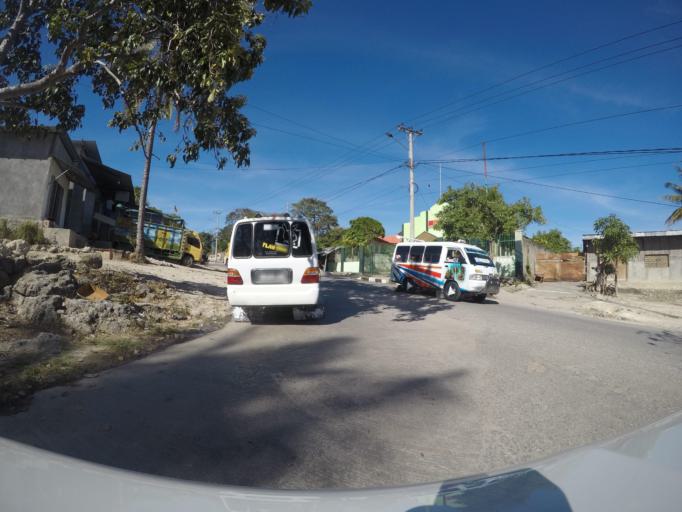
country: TL
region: Baucau
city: Baucau
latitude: -8.4681
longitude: 126.4593
